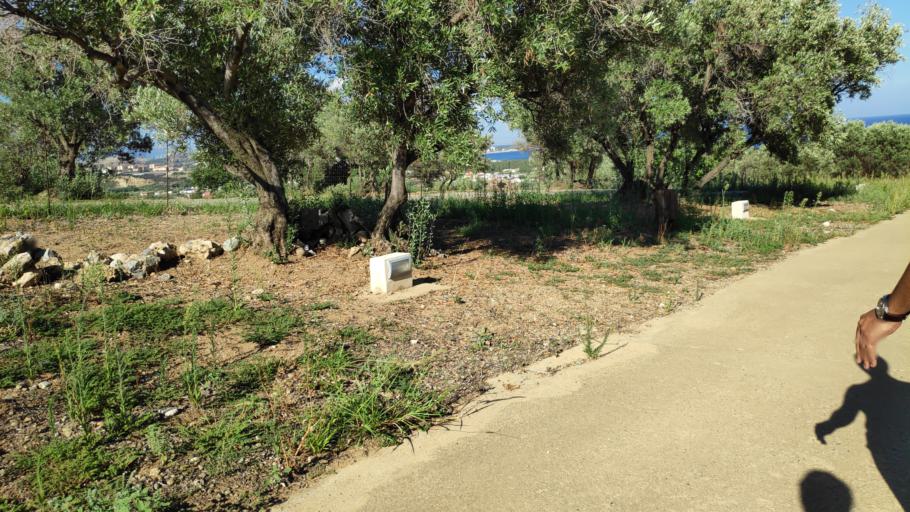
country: IT
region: Calabria
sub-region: Provincia di Catanzaro
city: Roccelletta
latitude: 38.8074
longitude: 16.5918
